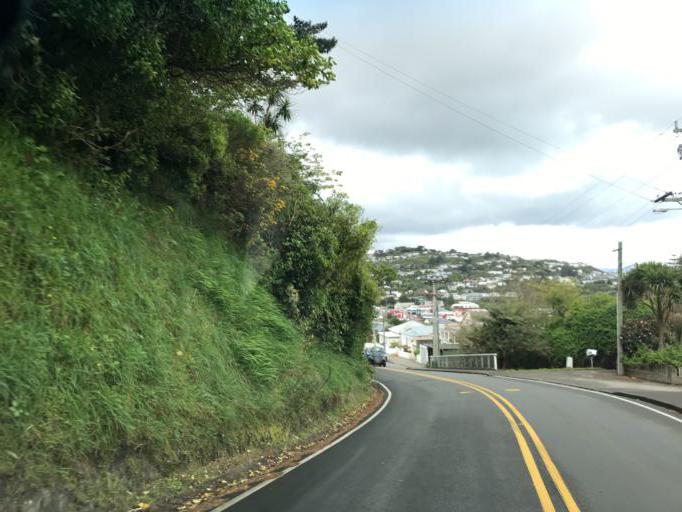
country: NZ
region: Wellington
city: Petone
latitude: -41.2186
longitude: 174.8011
